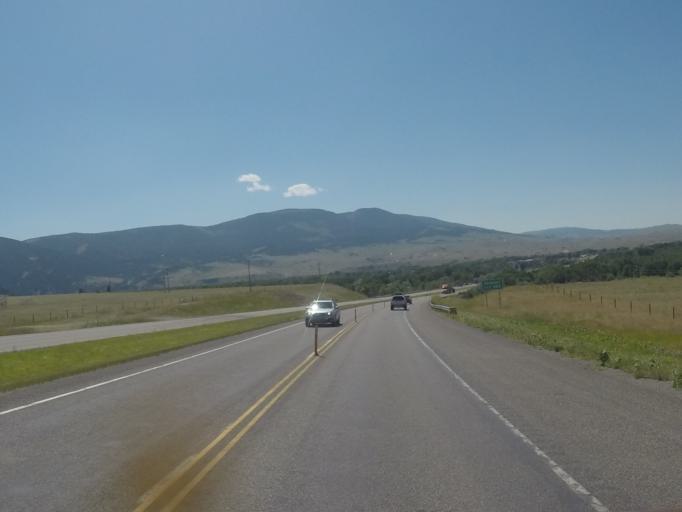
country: US
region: Montana
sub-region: Park County
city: Livingston
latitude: 45.6454
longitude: -110.5527
